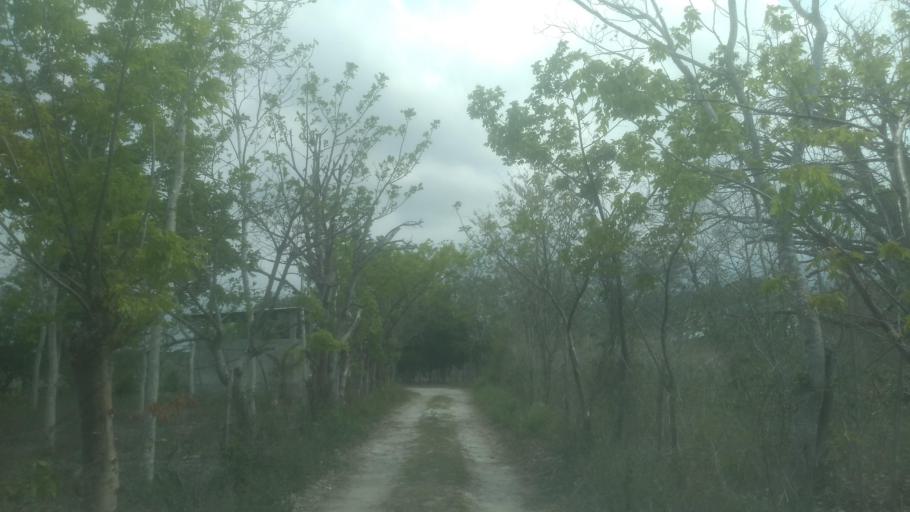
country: MX
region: Veracruz
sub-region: Emiliano Zapata
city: Plan del Rio
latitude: 19.3877
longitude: -96.6280
